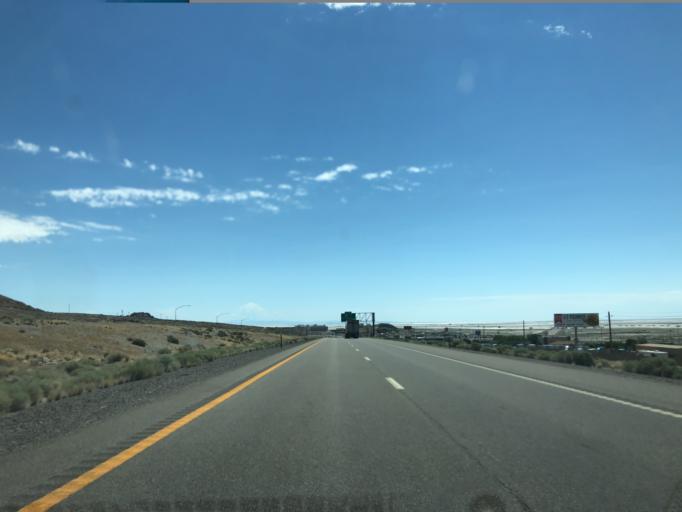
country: US
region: Nevada
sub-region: Elko County
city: West Wendover
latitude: 40.7422
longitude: -114.0661
